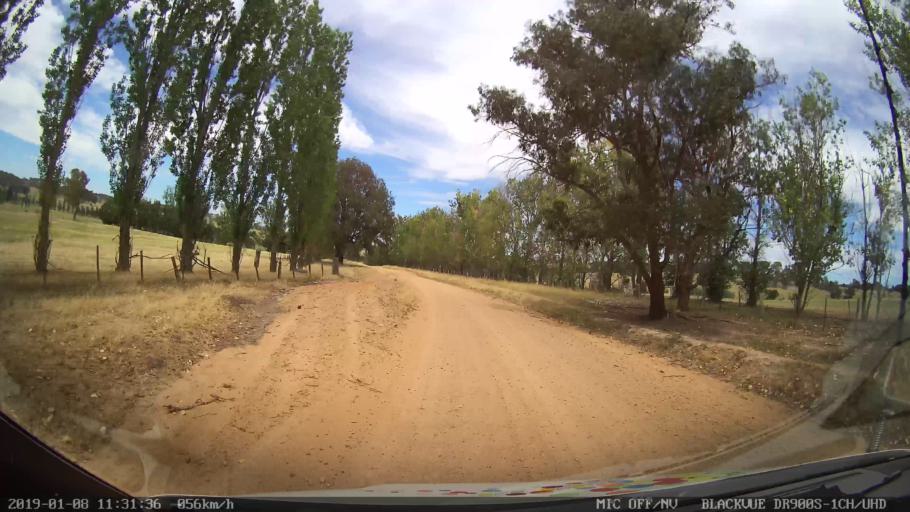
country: AU
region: New South Wales
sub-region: Guyra
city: Guyra
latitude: -30.3130
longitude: 151.5359
